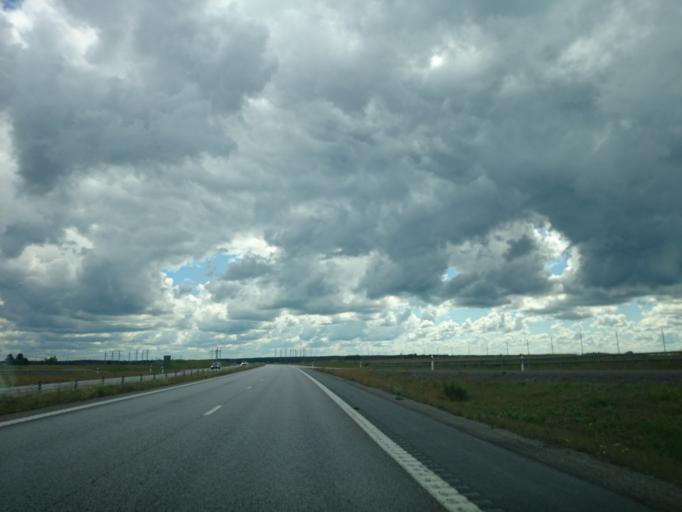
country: SE
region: Uppsala
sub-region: Tierps Kommun
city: Tierp
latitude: 60.3384
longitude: 17.4876
